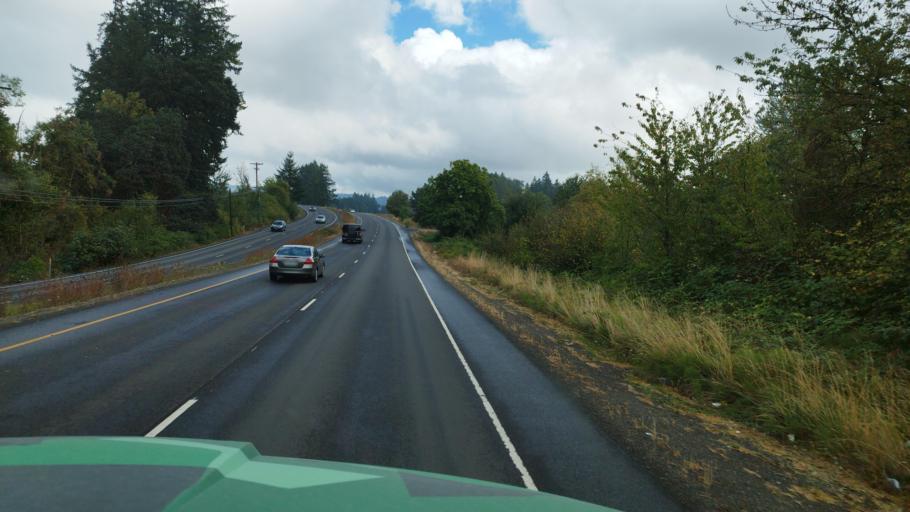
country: US
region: Oregon
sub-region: Yamhill County
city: Lafayette
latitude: 45.2414
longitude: -123.1356
